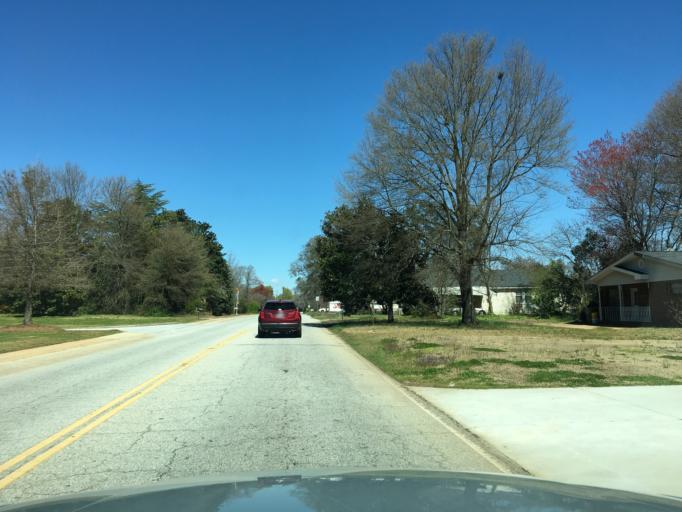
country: US
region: South Carolina
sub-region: Spartanburg County
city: Fairforest
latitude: 34.9267
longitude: -82.0013
